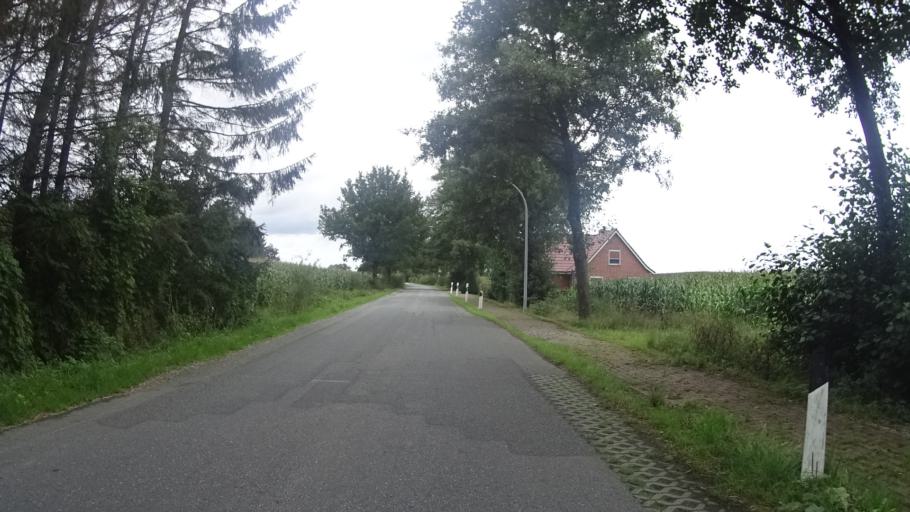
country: DE
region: Lower Saxony
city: Stinstedt
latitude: 53.6371
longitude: 8.9599
